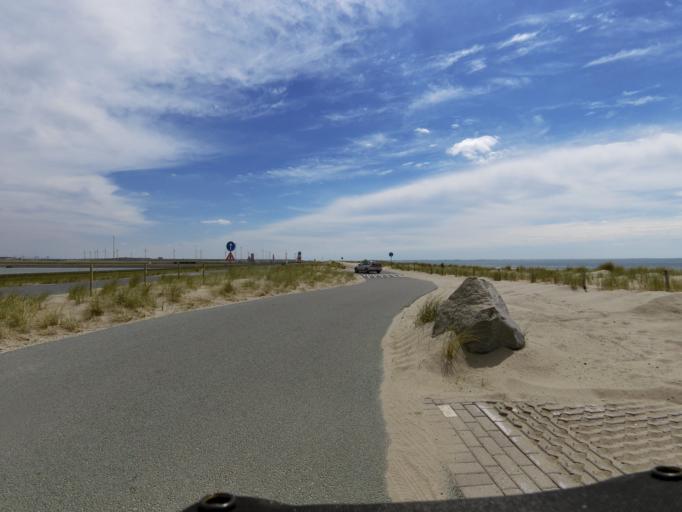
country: NL
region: South Holland
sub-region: Gemeente Goeree-Overflakkee
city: Goedereede
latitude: 51.9507
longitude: 3.9671
